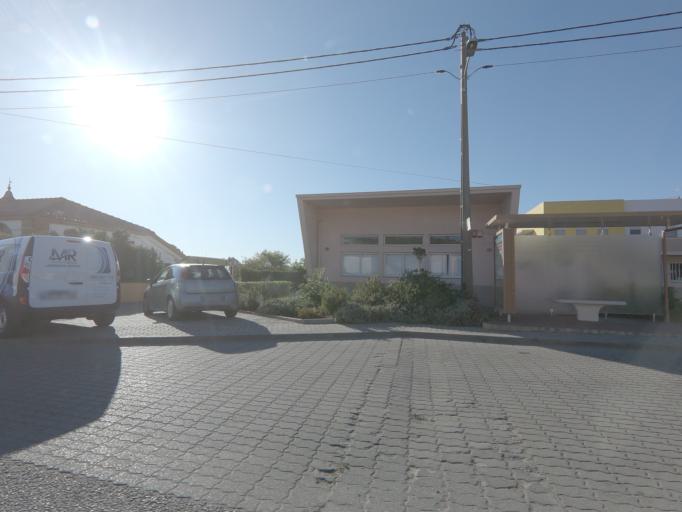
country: PT
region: Setubal
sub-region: Palmela
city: Quinta do Anjo
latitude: 38.5298
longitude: -8.9918
